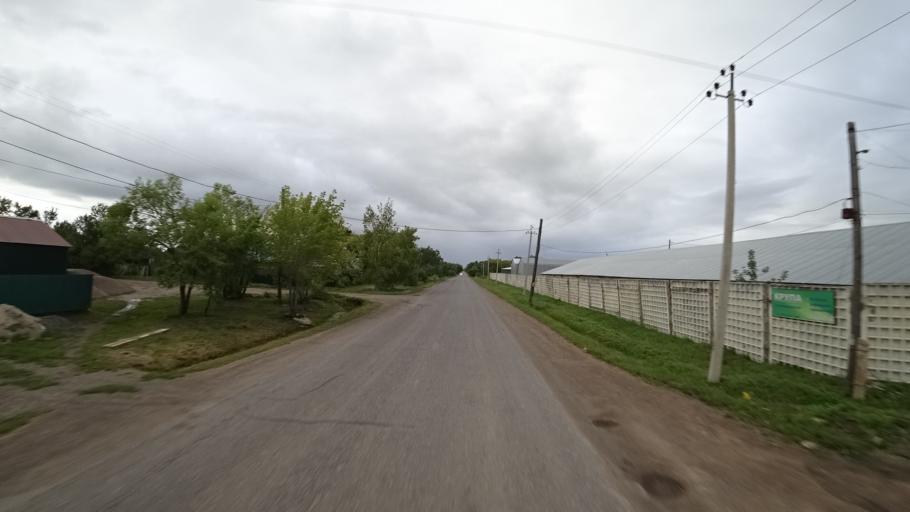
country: RU
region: Primorskiy
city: Chernigovka
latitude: 44.3360
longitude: 132.5906
